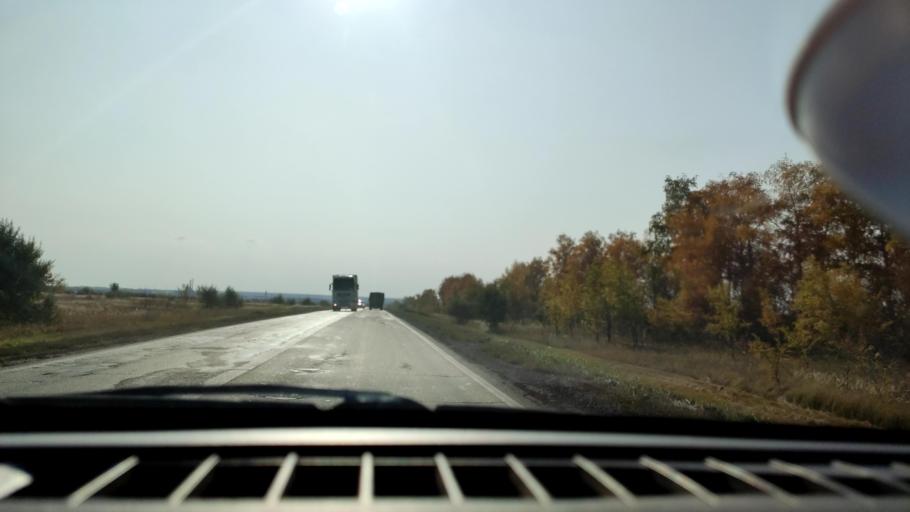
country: RU
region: Samara
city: Smyshlyayevka
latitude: 53.1144
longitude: 50.3592
